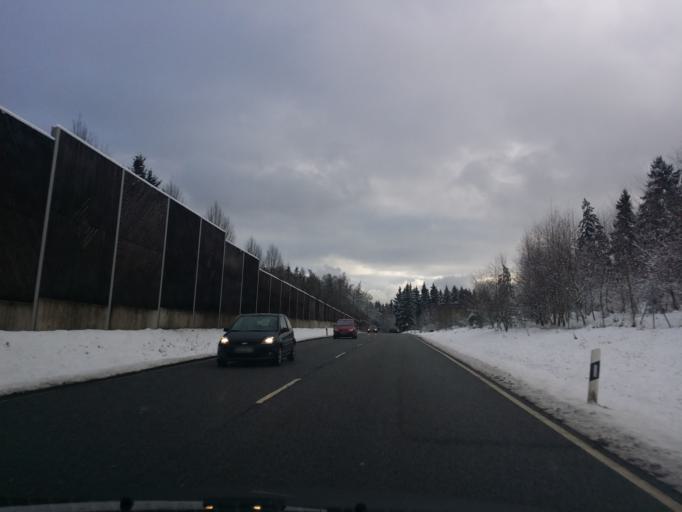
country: DE
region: Hesse
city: Taunusstein
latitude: 50.1532
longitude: 8.2125
